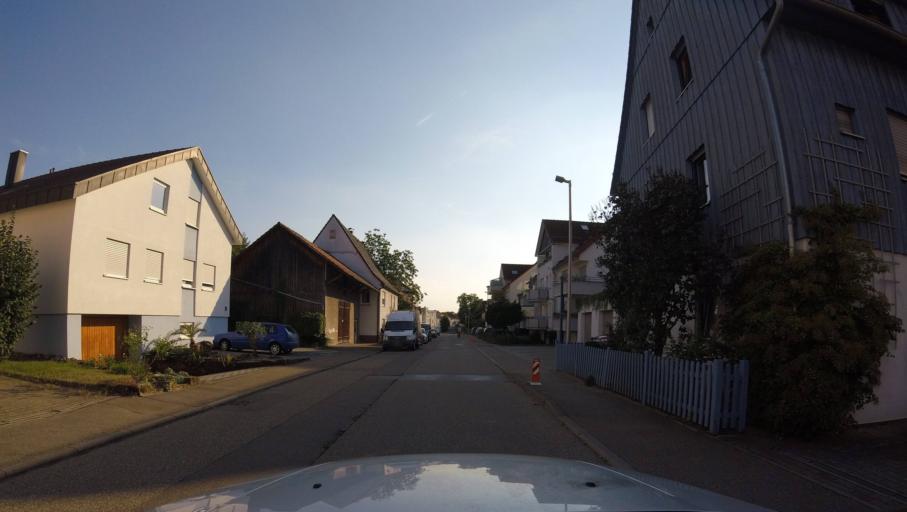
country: DE
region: Baden-Wuerttemberg
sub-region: Regierungsbezirk Stuttgart
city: Leutenbach
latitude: 48.9025
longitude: 9.4039
